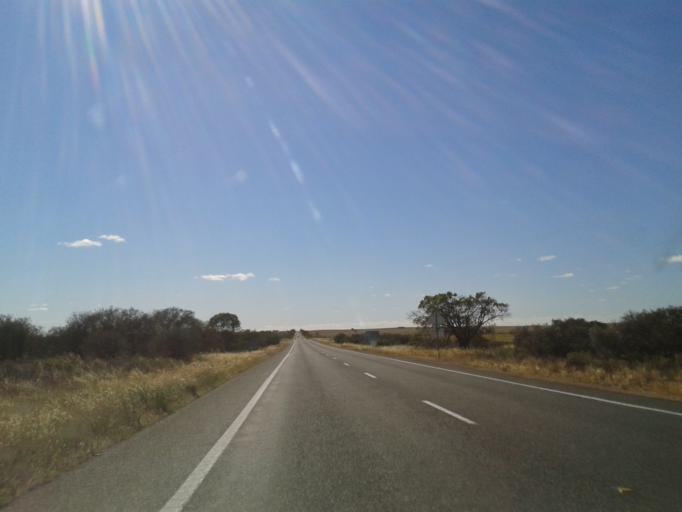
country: AU
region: South Australia
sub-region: Renmark Paringa
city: Renmark
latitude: -34.2750
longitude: 141.1597
